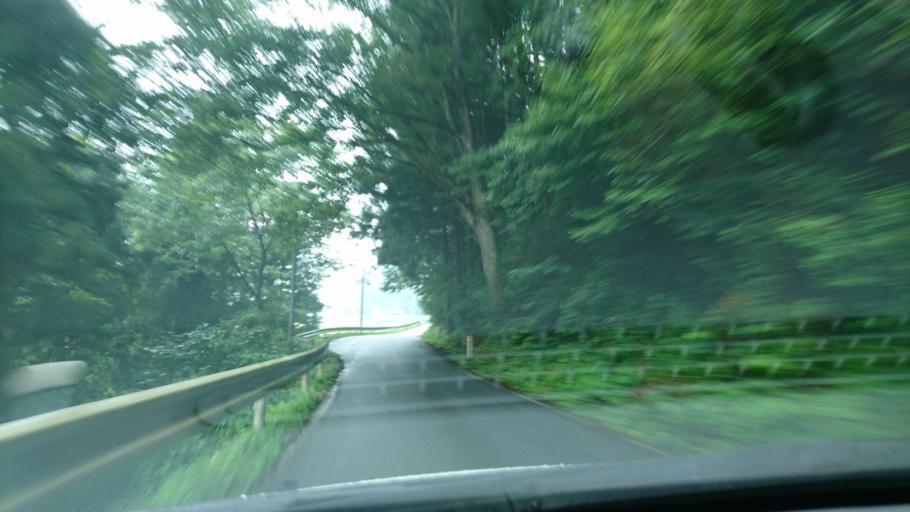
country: JP
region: Iwate
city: Ichinoseki
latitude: 38.8661
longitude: 141.2645
